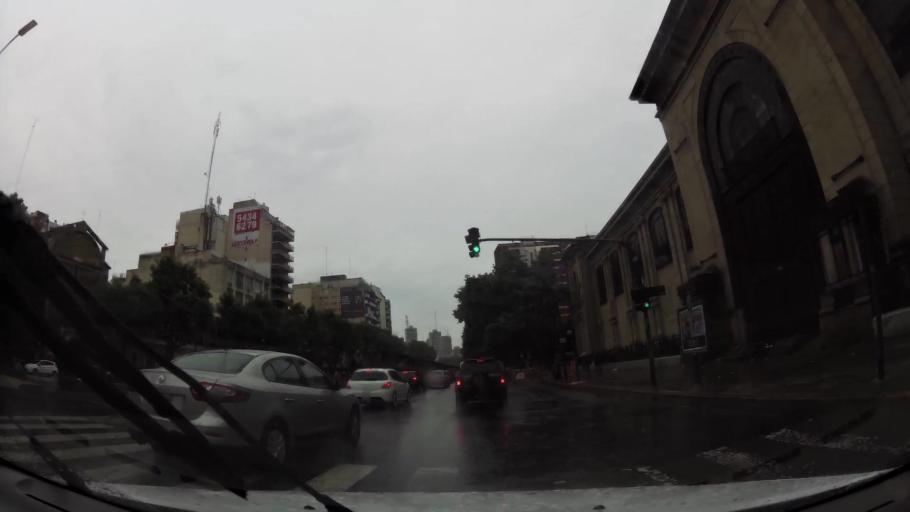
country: AR
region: Buenos Aires F.D.
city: Colegiales
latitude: -34.5805
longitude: -58.4222
